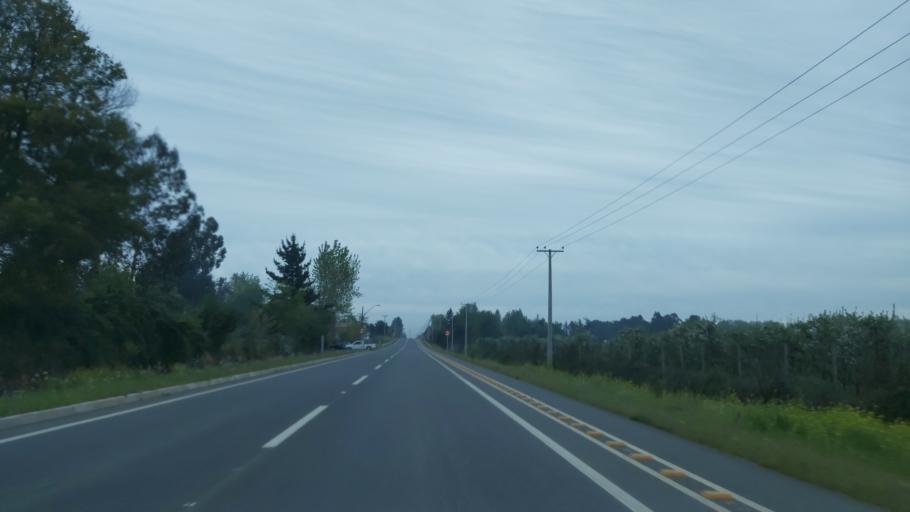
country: CL
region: Maule
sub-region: Provincia de Linares
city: Colbun
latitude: -35.6853
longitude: -71.4762
